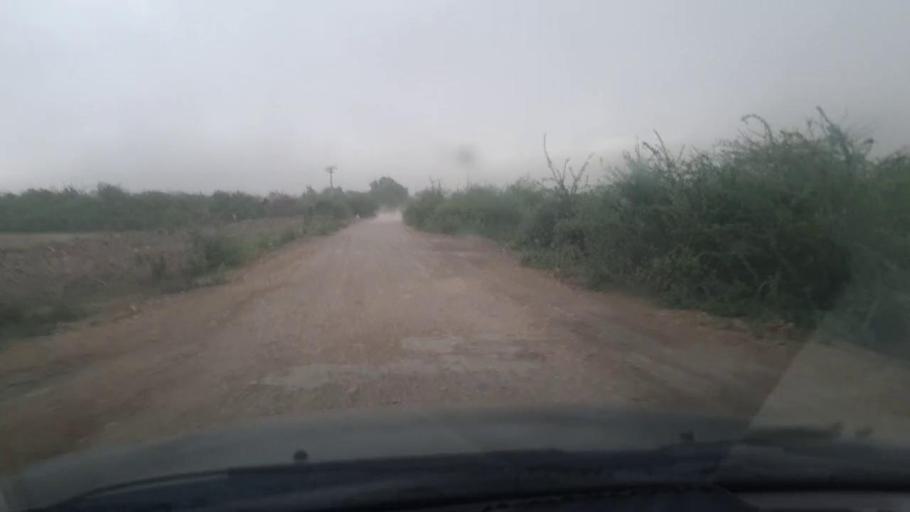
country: PK
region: Sindh
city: Digri
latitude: 25.0034
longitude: 69.0961
